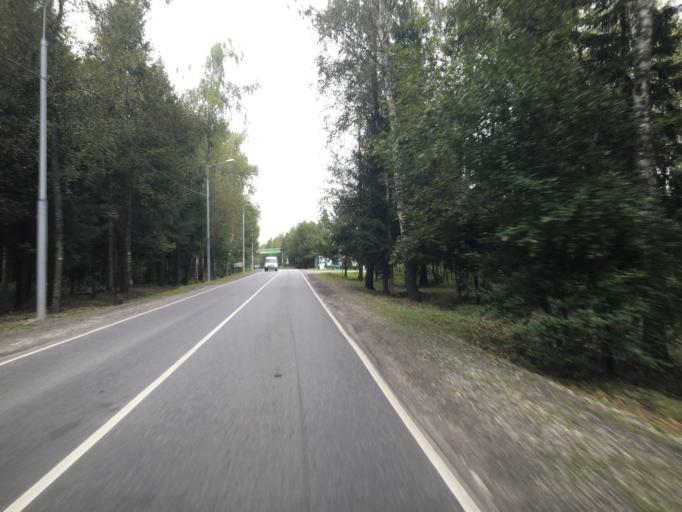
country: RU
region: Moskovskaya
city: Vatutinki
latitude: 55.5057
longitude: 37.3684
